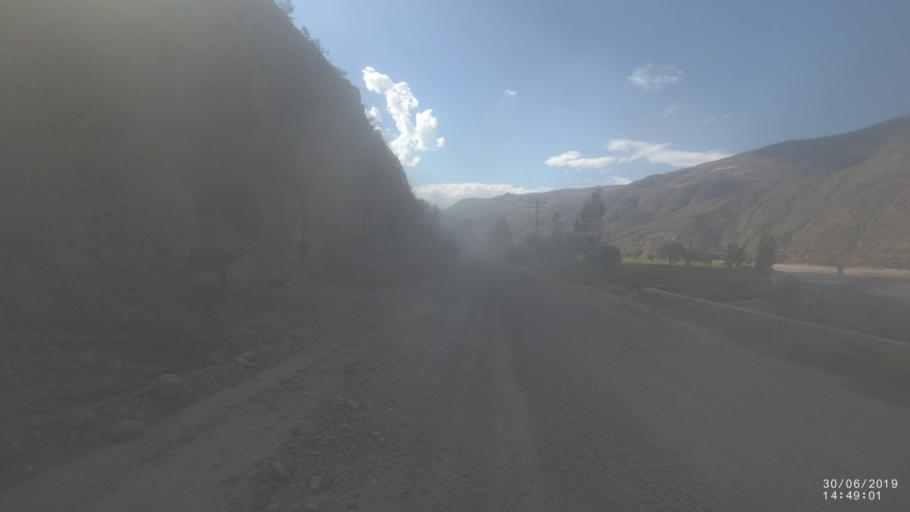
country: BO
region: Cochabamba
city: Irpa Irpa
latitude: -17.7859
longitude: -66.3416
